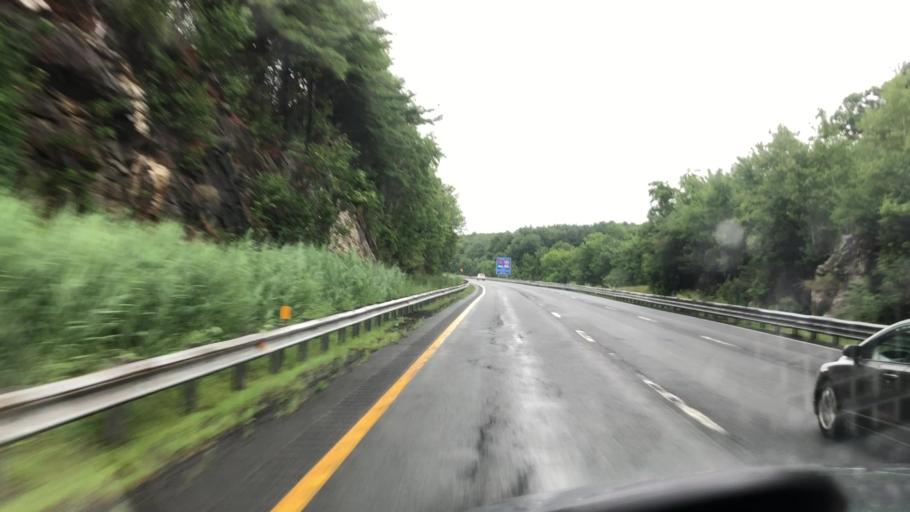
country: US
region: Massachusetts
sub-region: Hampden County
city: Granville
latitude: 42.1803
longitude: -72.9182
